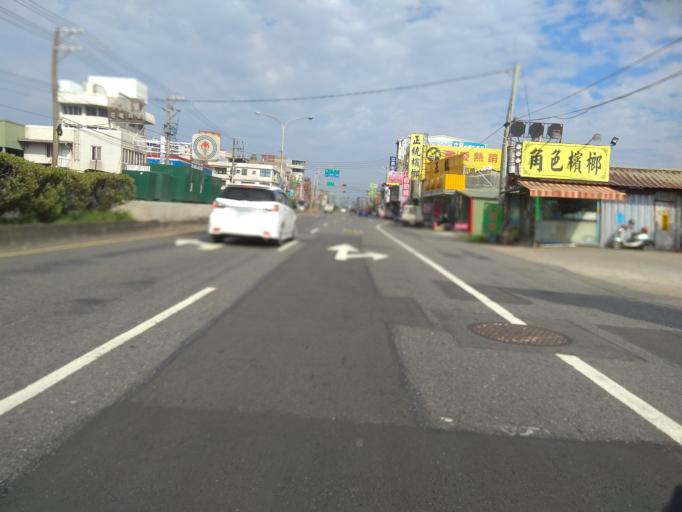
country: TW
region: Taiwan
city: Taoyuan City
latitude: 25.0639
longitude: 121.1801
